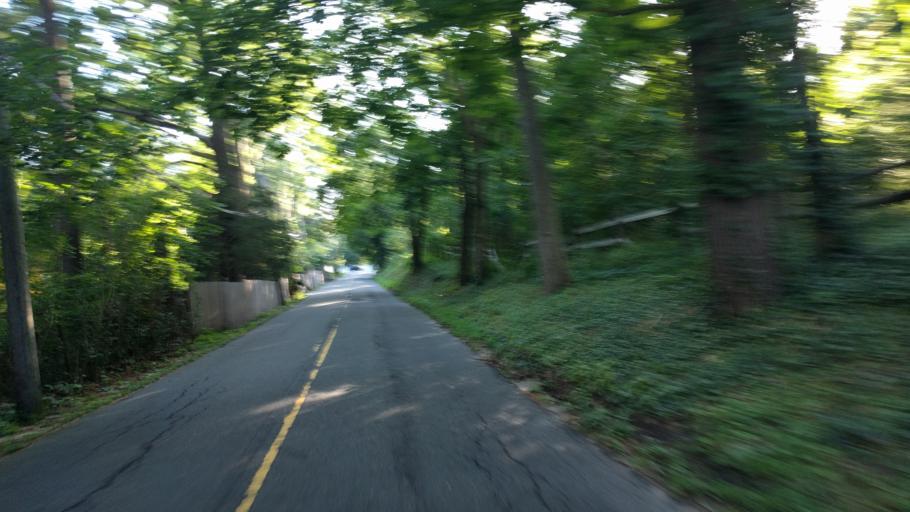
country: US
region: New York
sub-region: Nassau County
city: Locust Valley
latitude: 40.8720
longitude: -73.5707
